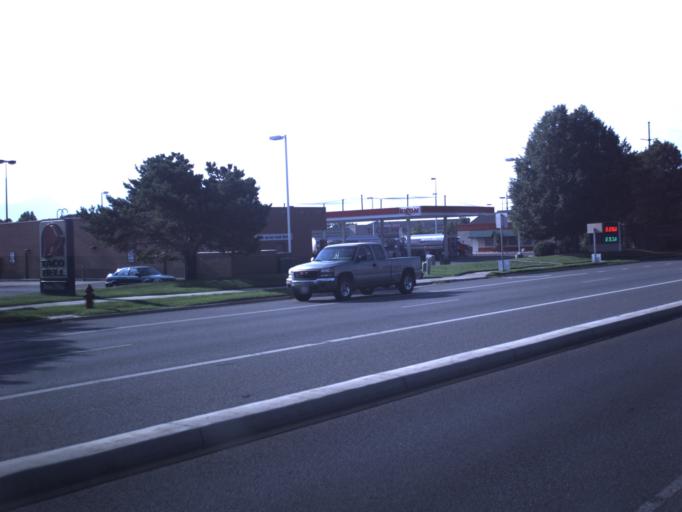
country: US
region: Utah
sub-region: Utah County
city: American Fork
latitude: 40.3640
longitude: -111.7856
